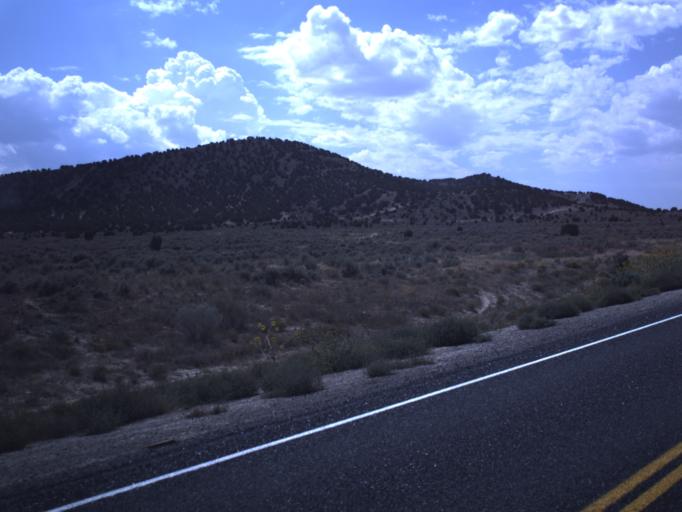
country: US
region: Utah
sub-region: Utah County
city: Eagle Mountain
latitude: 40.2344
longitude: -112.1690
